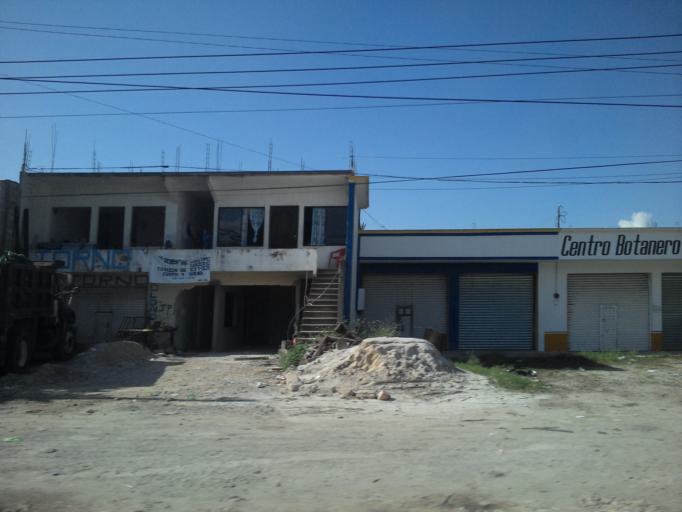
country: MX
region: Chiapas
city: Palenque
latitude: 17.5429
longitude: -91.9877
